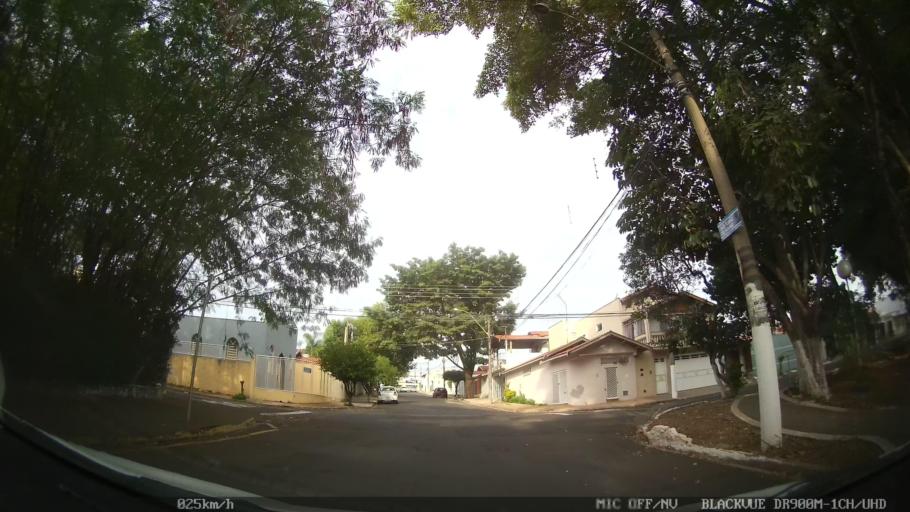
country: BR
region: Sao Paulo
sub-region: Piracicaba
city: Piracicaba
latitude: -22.7373
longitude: -47.6250
